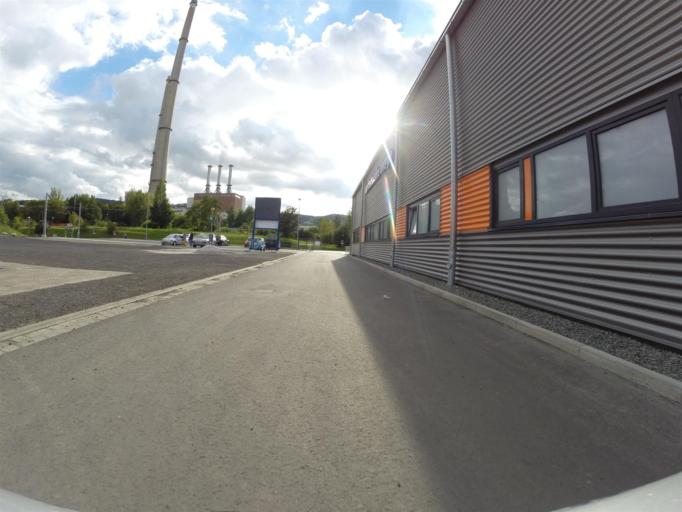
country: DE
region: Thuringia
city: Jena
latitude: 50.8997
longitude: 11.5889
